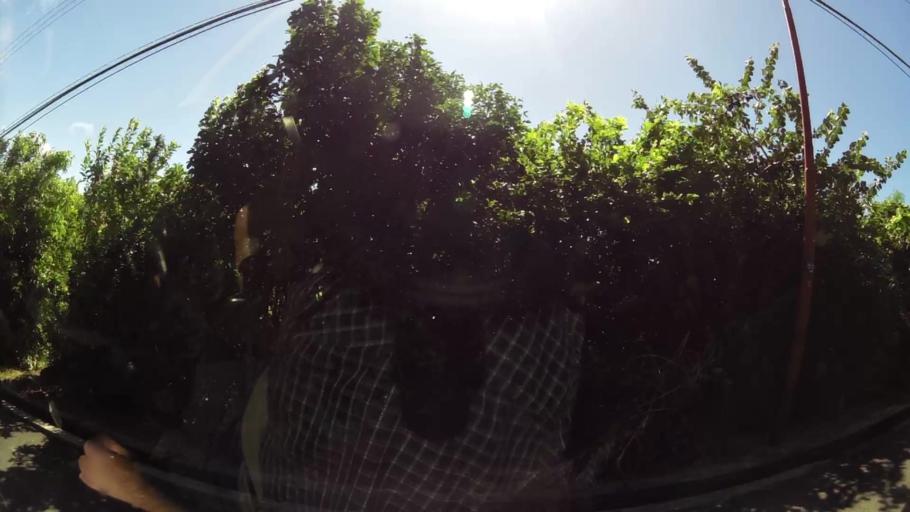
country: TT
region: Tobago
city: Scarborough
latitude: 11.1691
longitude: -60.7568
